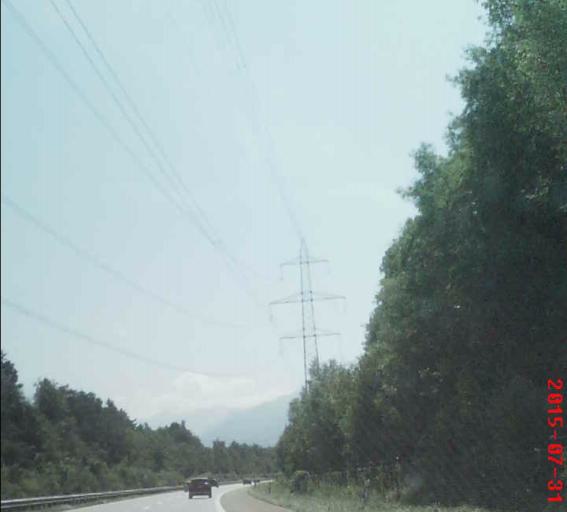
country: LI
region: Ruggell
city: Ruggell
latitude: 47.2617
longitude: 9.5277
